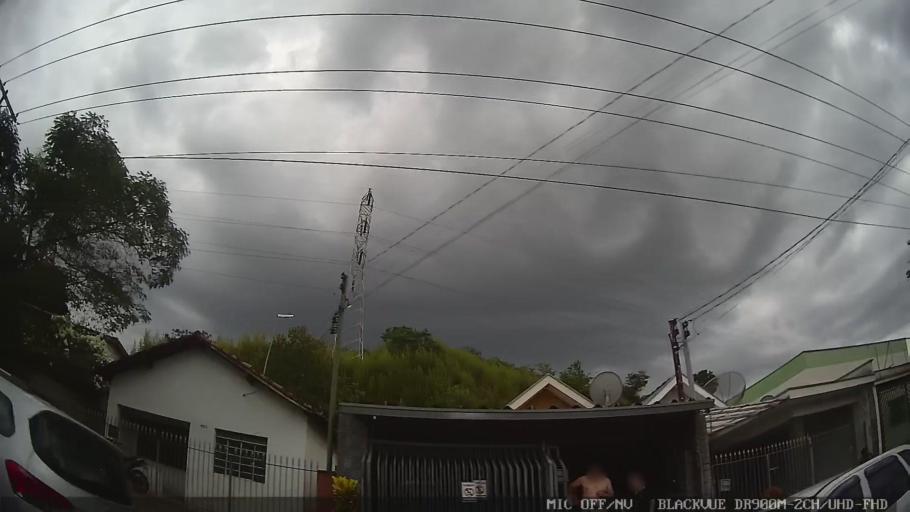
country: BR
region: Sao Paulo
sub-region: Amparo
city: Amparo
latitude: -22.7107
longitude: -46.7859
